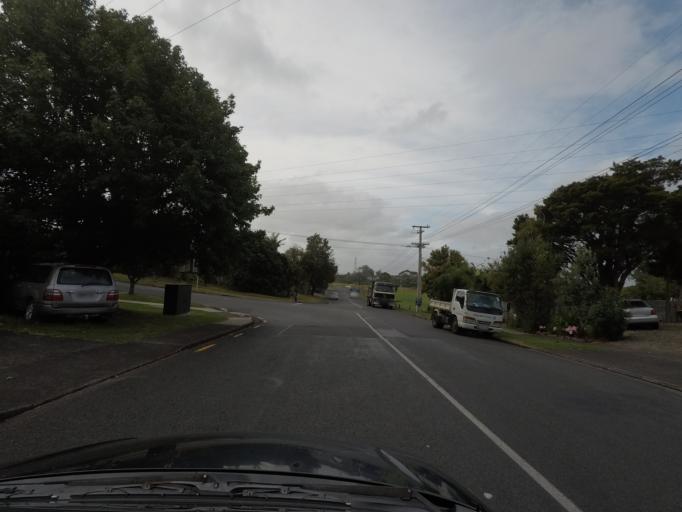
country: NZ
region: Auckland
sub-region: Auckland
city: Rosebank
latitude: -36.8958
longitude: 174.6688
